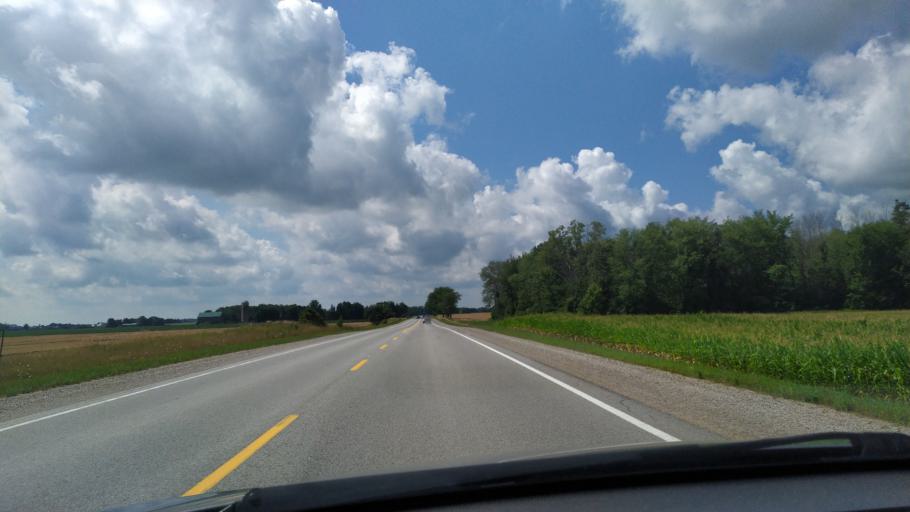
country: CA
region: Ontario
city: South Huron
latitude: 43.2757
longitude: -81.3538
